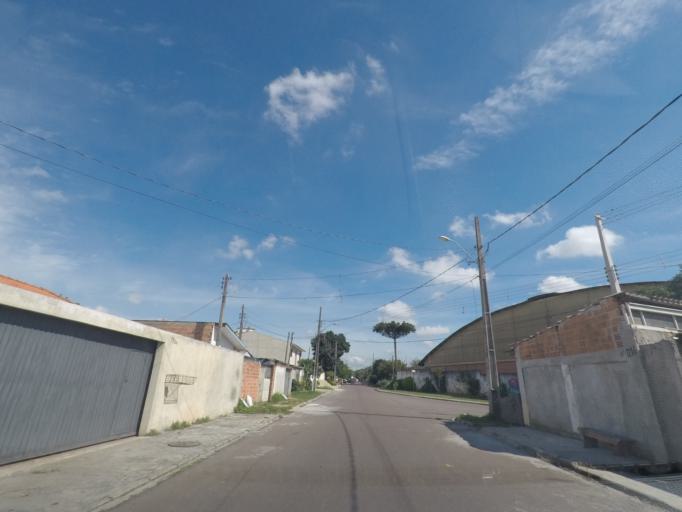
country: BR
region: Parana
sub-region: Curitiba
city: Curitiba
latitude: -25.4699
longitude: -49.2659
